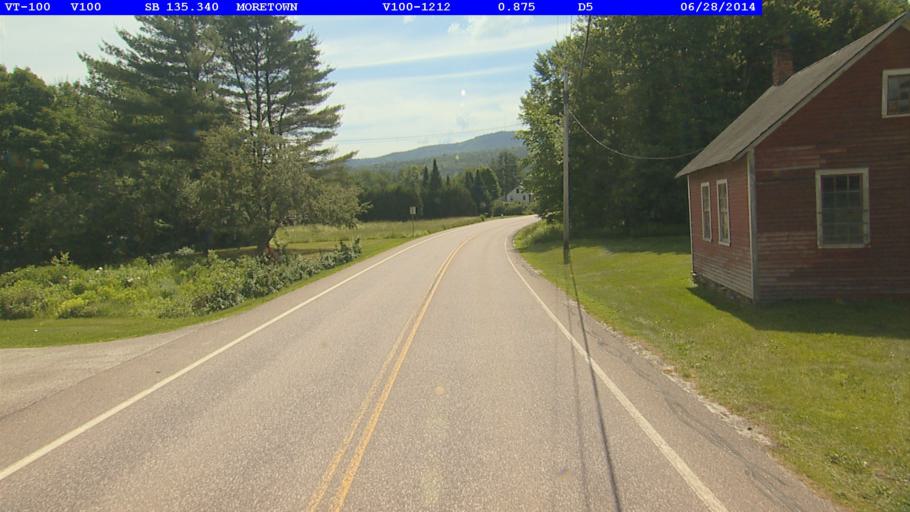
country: US
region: Vermont
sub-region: Washington County
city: Waterbury
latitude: 44.2439
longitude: -72.7820
